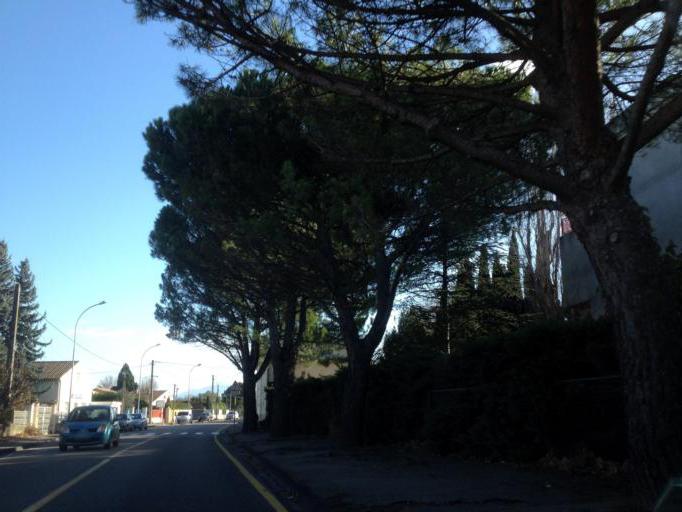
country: FR
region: Provence-Alpes-Cote d'Azur
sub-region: Departement du Vaucluse
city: Orange
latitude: 44.1352
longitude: 4.8212
